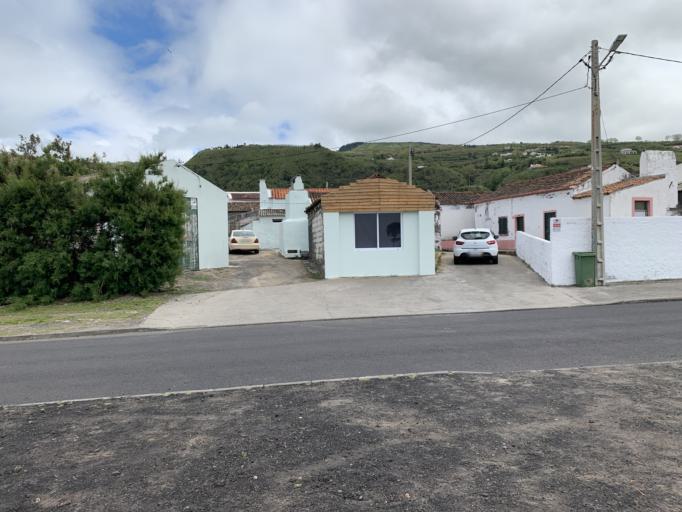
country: PT
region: Azores
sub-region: Ponta Delgada
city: Arrifes
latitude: 37.8912
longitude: -25.8249
